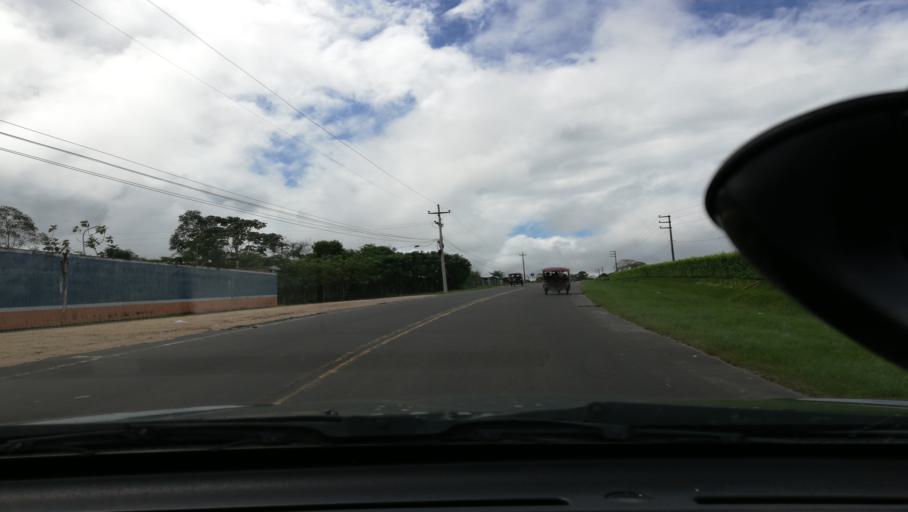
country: PE
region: Loreto
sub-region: Provincia de Maynas
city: Iquitos
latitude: -3.8656
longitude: -73.3413
